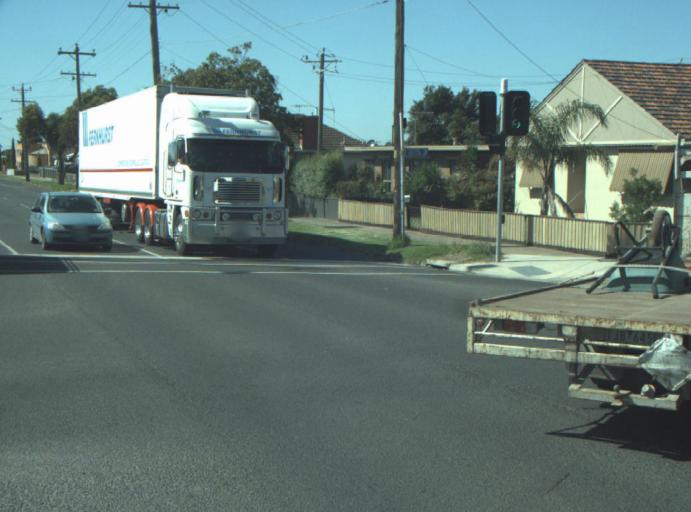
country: AU
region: Victoria
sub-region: Greater Geelong
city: Hamlyn Heights
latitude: -38.1159
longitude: 144.3303
